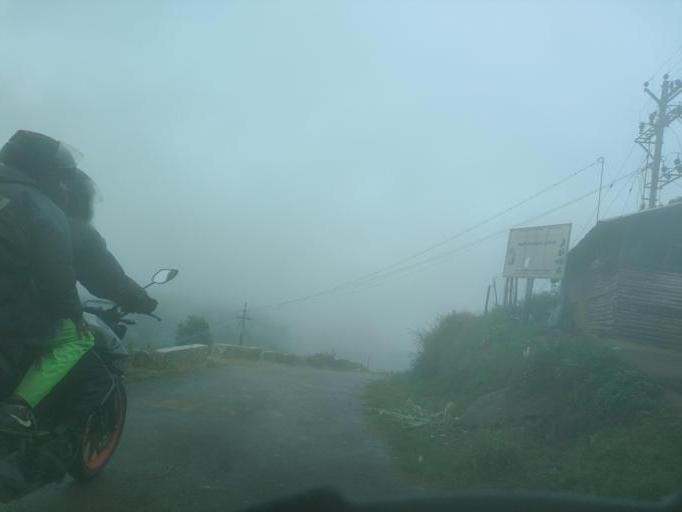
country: IN
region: Tamil Nadu
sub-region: Dindigul
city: Kodaikanal
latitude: 10.2338
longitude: 77.3285
